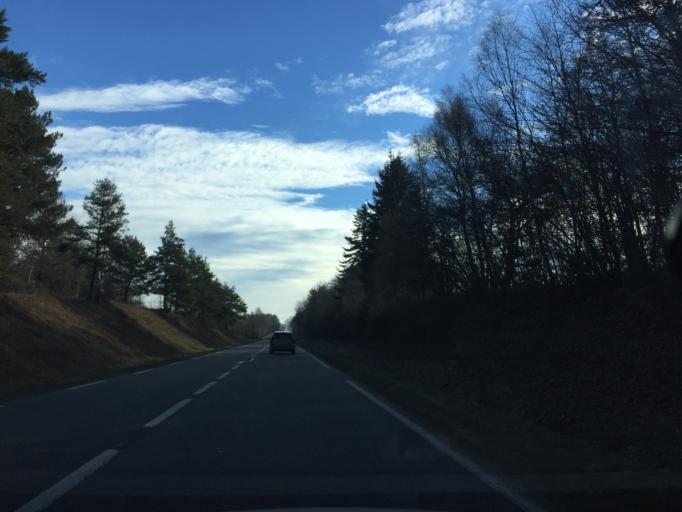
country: FR
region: Auvergne
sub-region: Departement du Puy-de-Dome
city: Gelles
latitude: 45.8535
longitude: 2.6899
